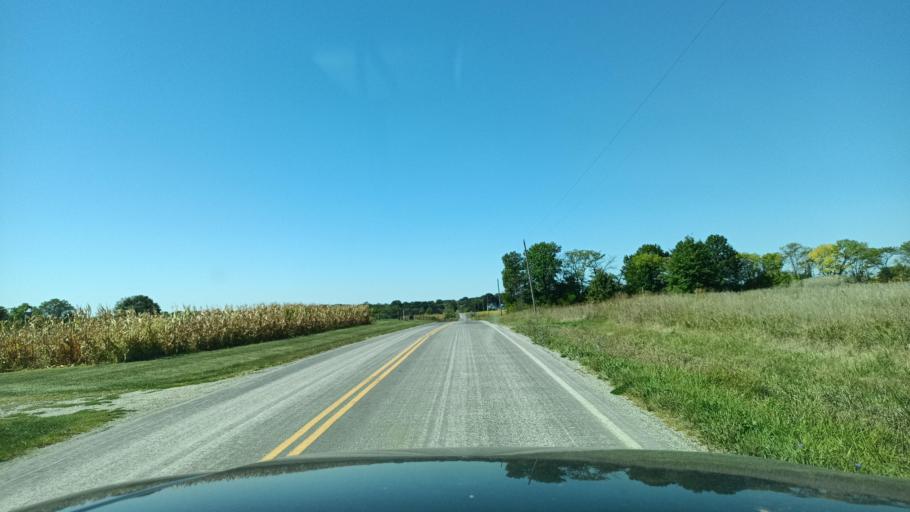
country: US
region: Missouri
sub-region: Macon County
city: La Plata
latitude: 40.0230
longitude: -92.5785
